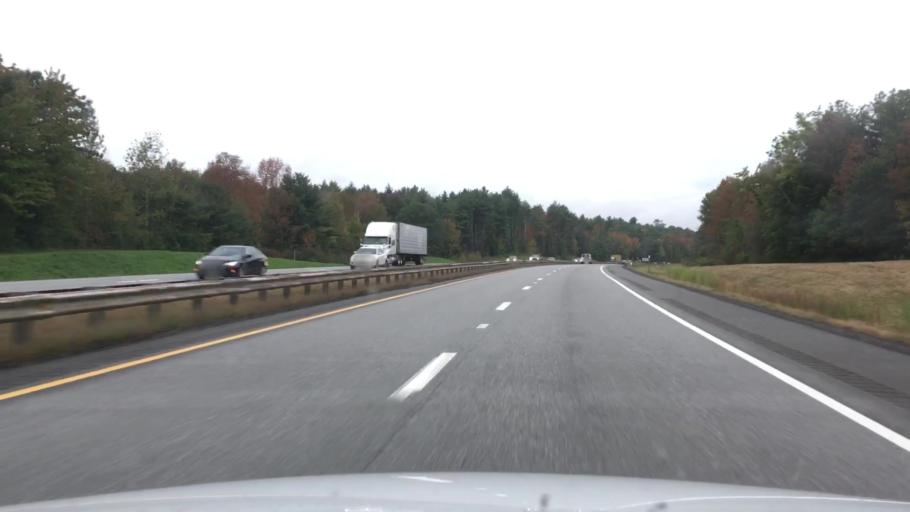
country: US
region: Maine
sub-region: Cumberland County
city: Cumberland Center
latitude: 43.7626
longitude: -70.3103
